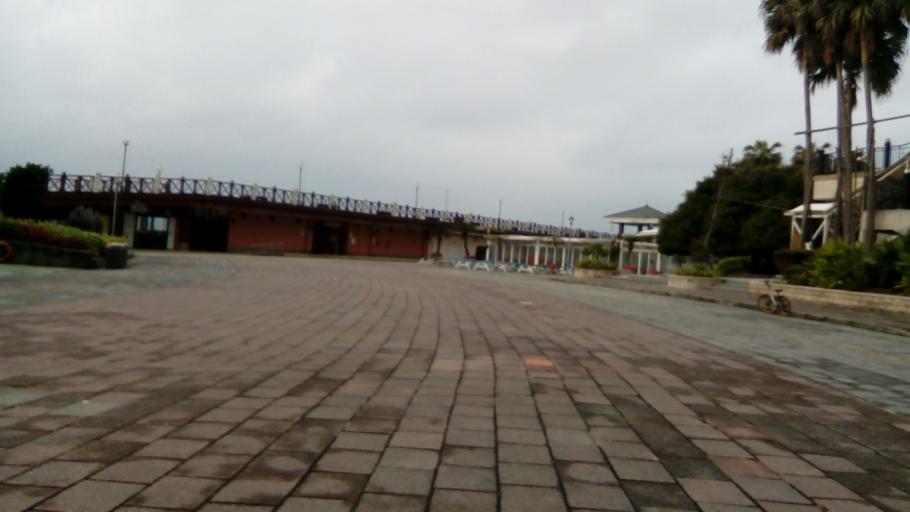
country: TW
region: Taipei
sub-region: Taipei
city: Banqiao
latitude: 25.1821
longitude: 121.4143
